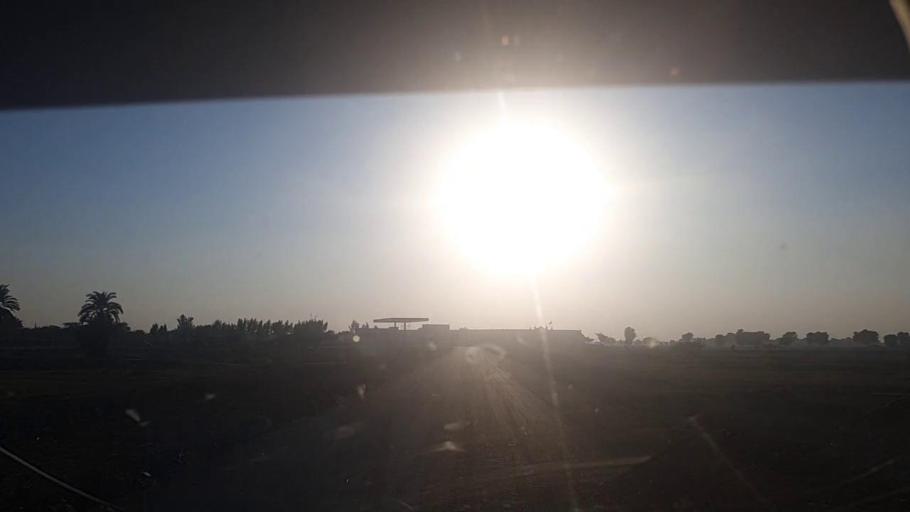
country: PK
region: Sindh
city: Hingorja
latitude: 27.2195
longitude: 68.4041
